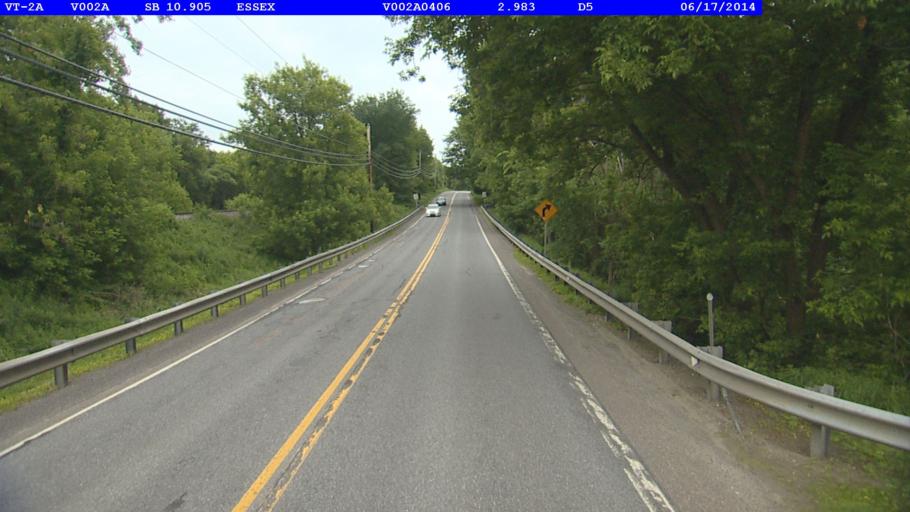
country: US
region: Vermont
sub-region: Chittenden County
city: Colchester
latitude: 44.5222
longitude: -73.1239
